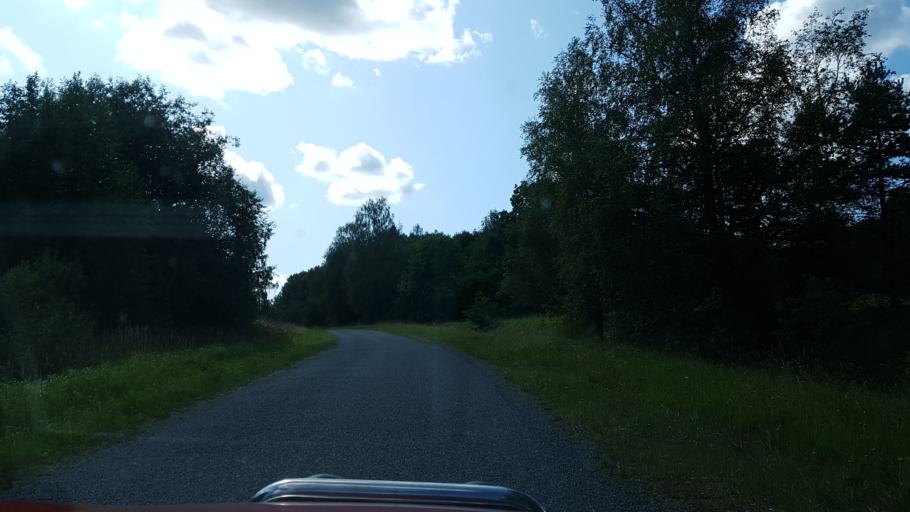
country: LV
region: Aluksnes Rajons
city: Aluksne
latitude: 57.6063
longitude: 27.1069
